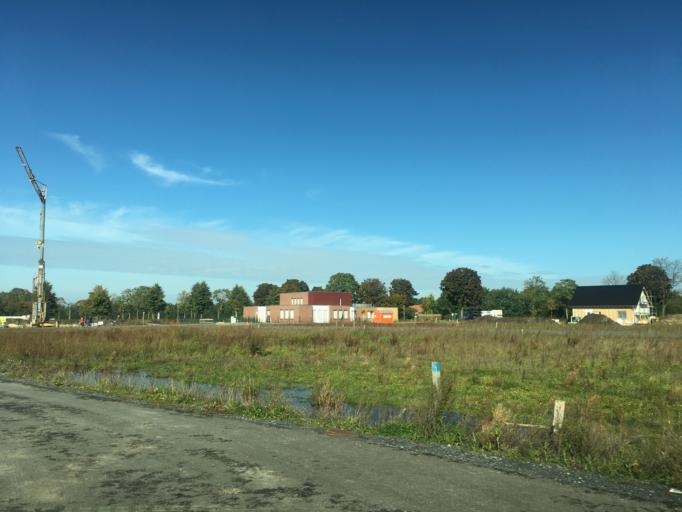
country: DE
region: North Rhine-Westphalia
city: Ludinghausen
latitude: 51.7810
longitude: 7.4651
